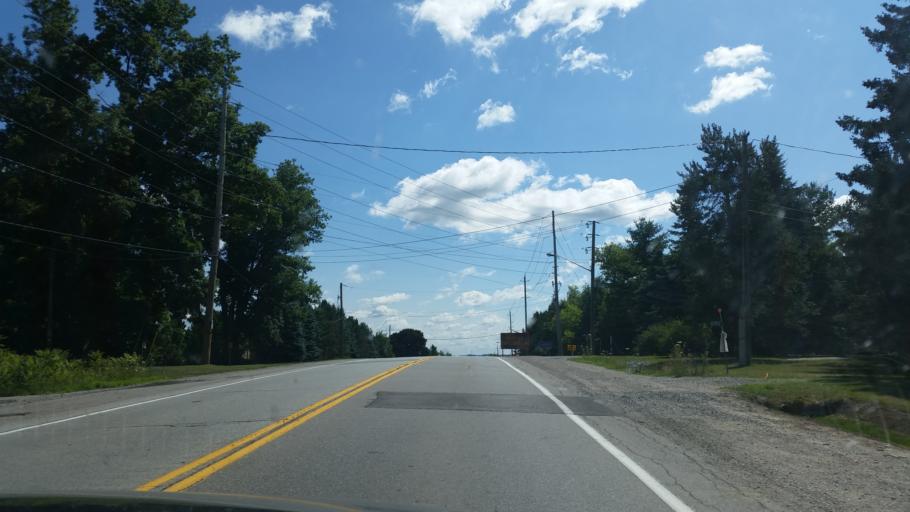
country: CA
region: Ontario
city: Vaughan
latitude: 43.8993
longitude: -79.6658
